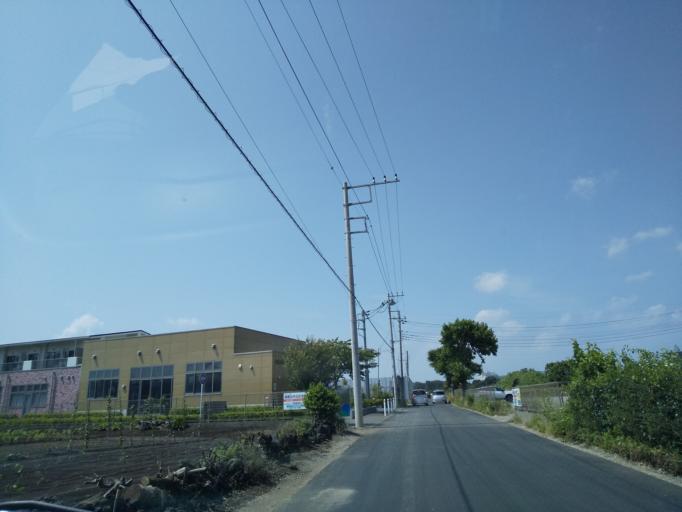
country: JP
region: Kanagawa
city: Zama
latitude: 35.5207
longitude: 139.3891
